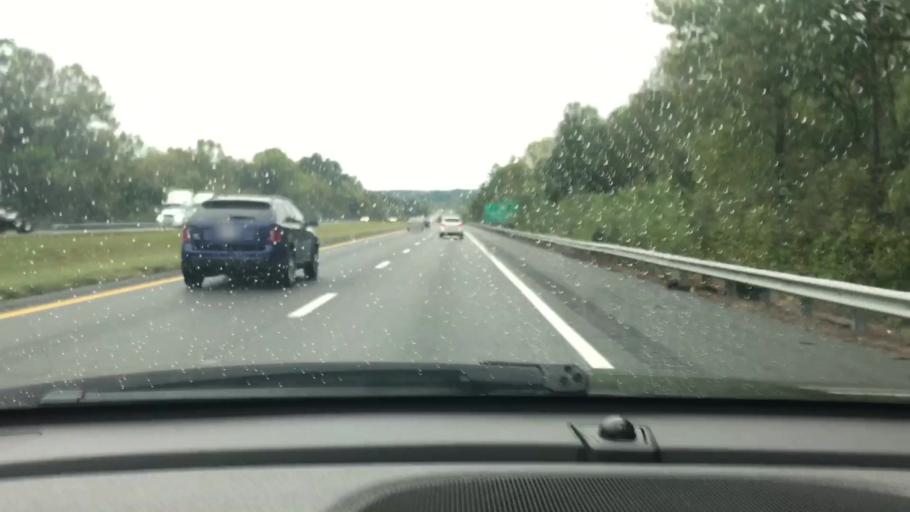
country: US
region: Tennessee
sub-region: Cheatham County
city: Pegram
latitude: 36.0873
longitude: -87.0758
